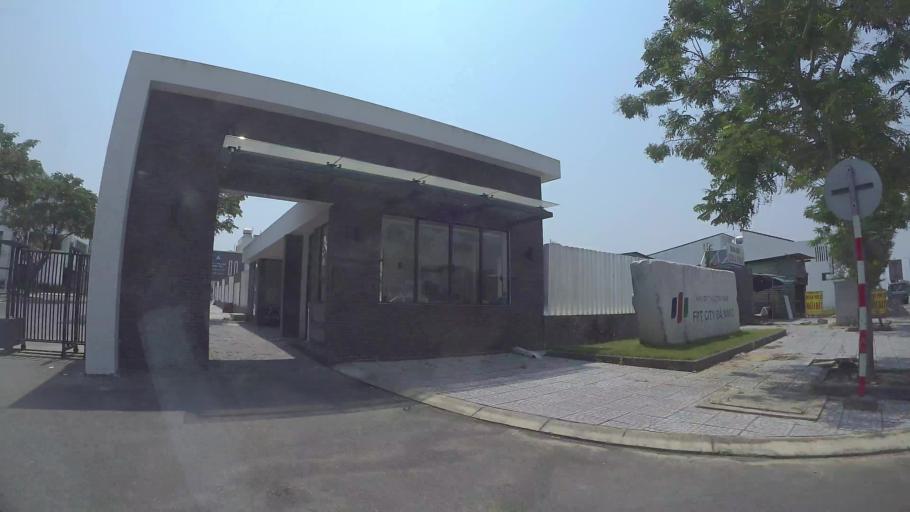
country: VN
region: Da Nang
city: Ngu Hanh Son
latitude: 15.9778
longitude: 108.2609
